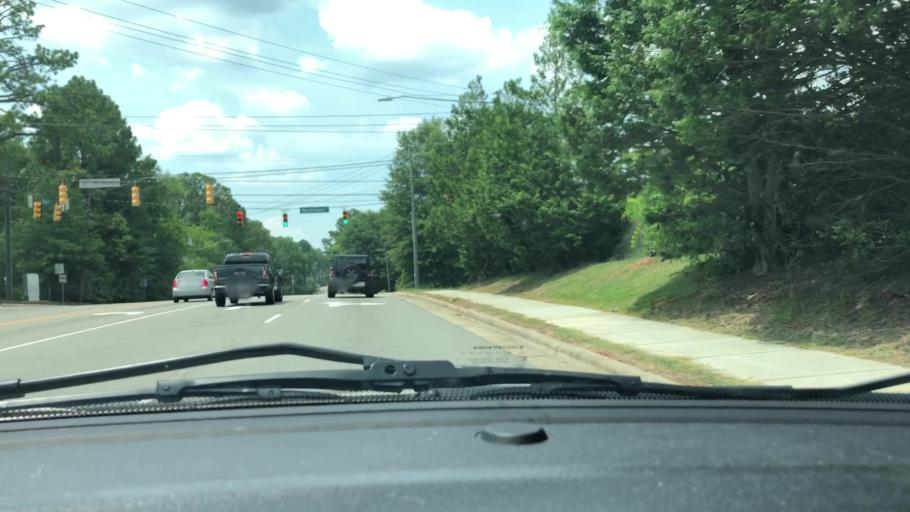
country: US
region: North Carolina
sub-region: Lee County
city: Sanford
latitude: 35.4852
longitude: -79.1850
